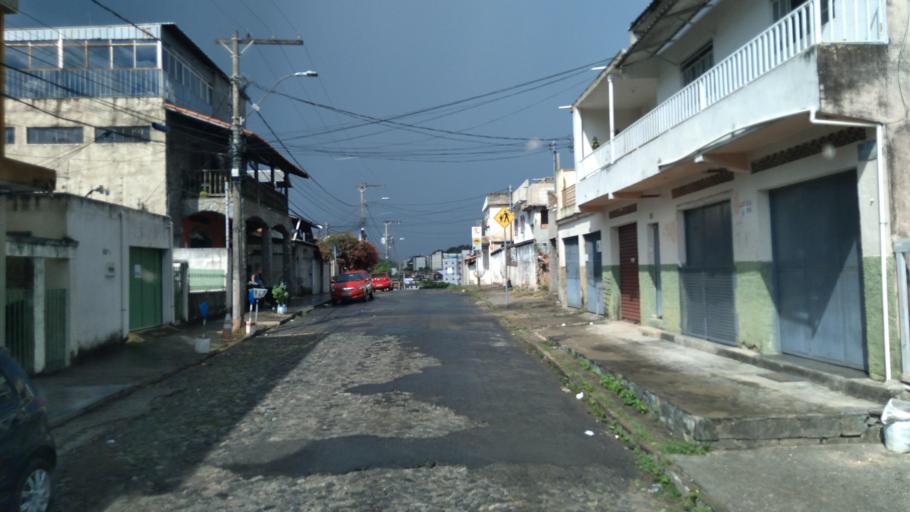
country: BR
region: Minas Gerais
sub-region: Contagem
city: Contagem
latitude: -19.9211
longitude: -44.0123
